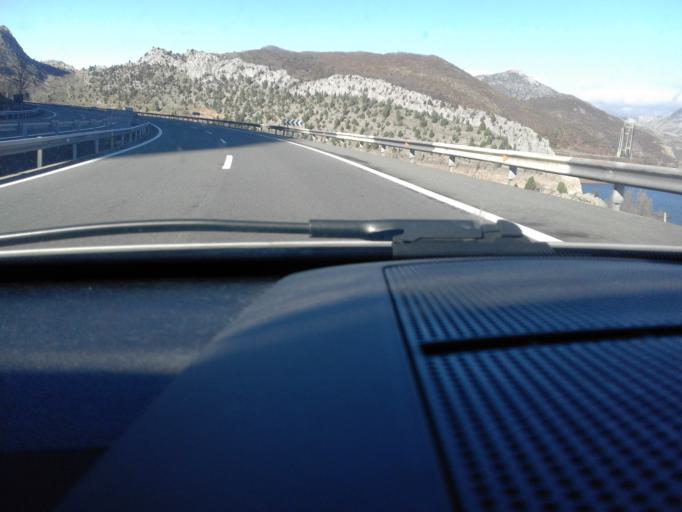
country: ES
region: Castille and Leon
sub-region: Provincia de Leon
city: Sena de Luna
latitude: 42.8790
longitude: -5.8816
